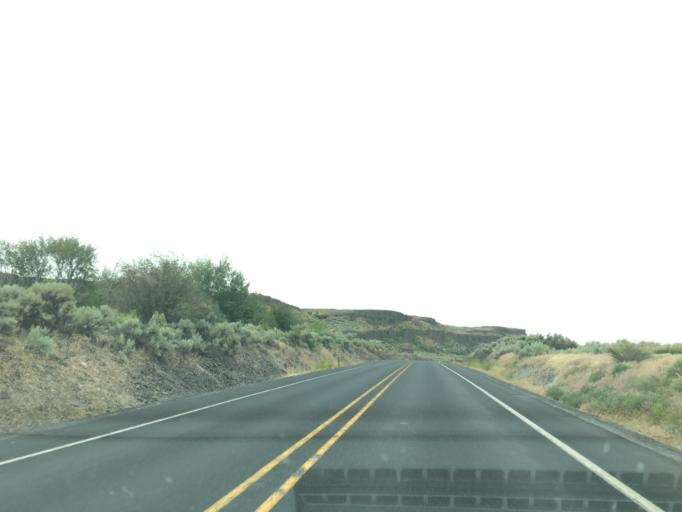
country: US
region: Washington
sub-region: Okanogan County
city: Coulee Dam
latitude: 47.7387
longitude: -119.2354
